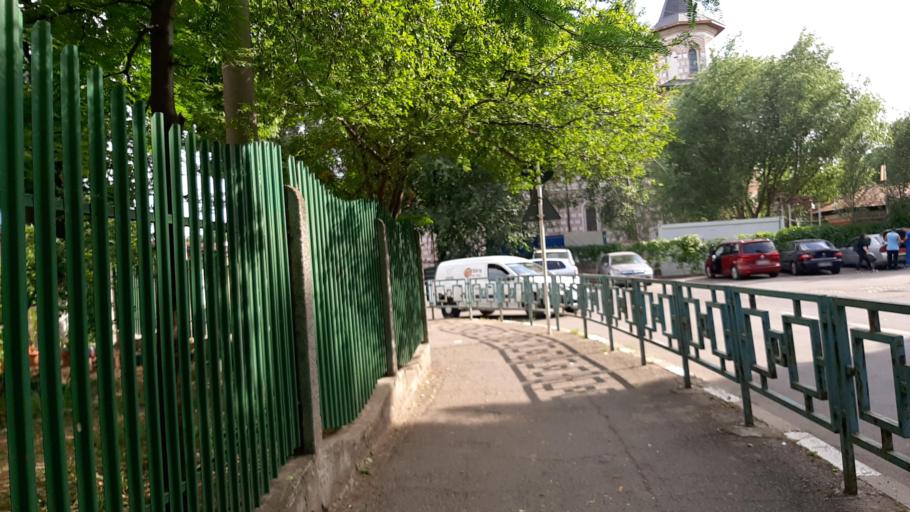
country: RO
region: Galati
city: Galati
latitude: 45.4420
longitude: 28.0264
